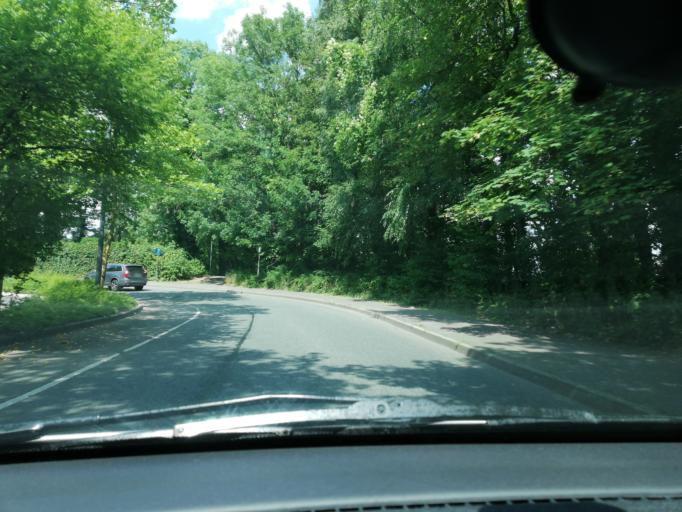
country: DE
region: North Rhine-Westphalia
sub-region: Regierungsbezirk Dusseldorf
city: Wuppertal
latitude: 51.2525
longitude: 7.1606
